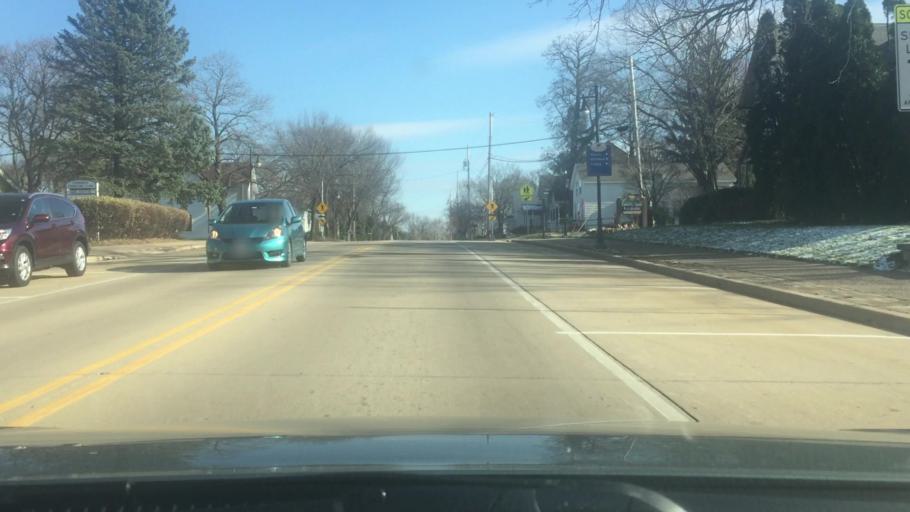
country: US
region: Wisconsin
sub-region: Jefferson County
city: Cambridge
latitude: 43.0034
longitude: -89.0158
